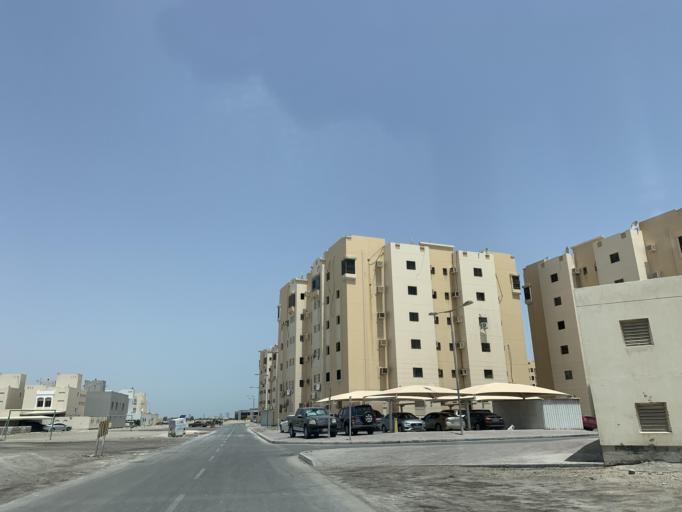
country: BH
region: Northern
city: Sitrah
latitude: 26.1410
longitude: 50.5956
